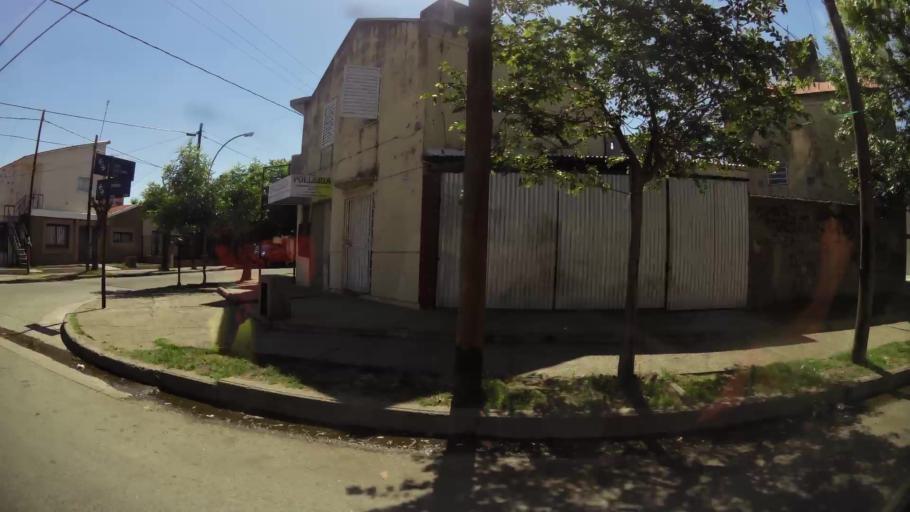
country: AR
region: Cordoba
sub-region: Departamento de Capital
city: Cordoba
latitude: -31.3753
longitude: -64.1590
